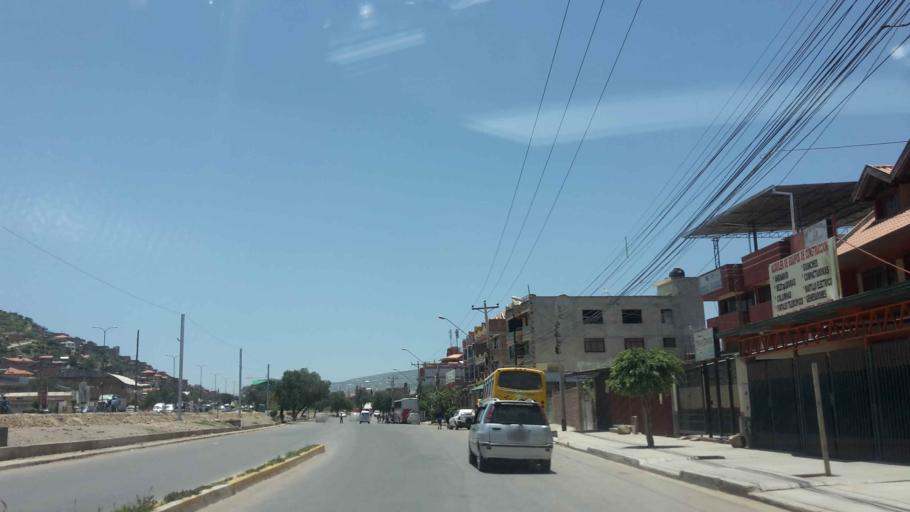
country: BO
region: Cochabamba
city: Cochabamba
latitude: -17.4303
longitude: -66.1514
